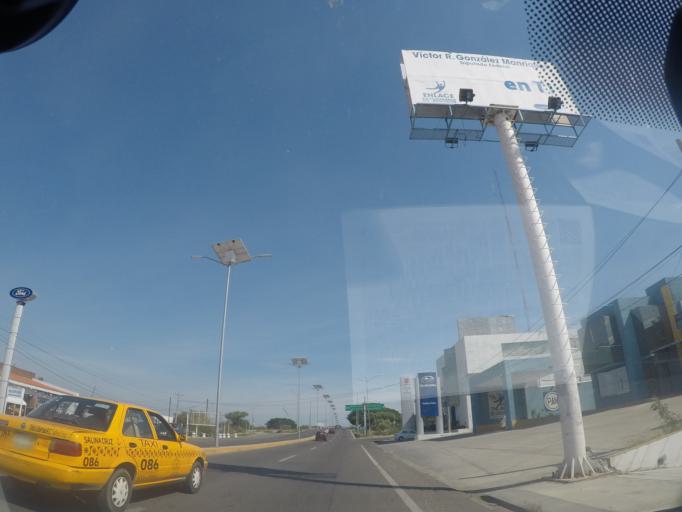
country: MX
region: Oaxaca
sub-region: Santo Domingo Tehuantepec
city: La Noria
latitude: 16.2242
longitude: -95.2093
